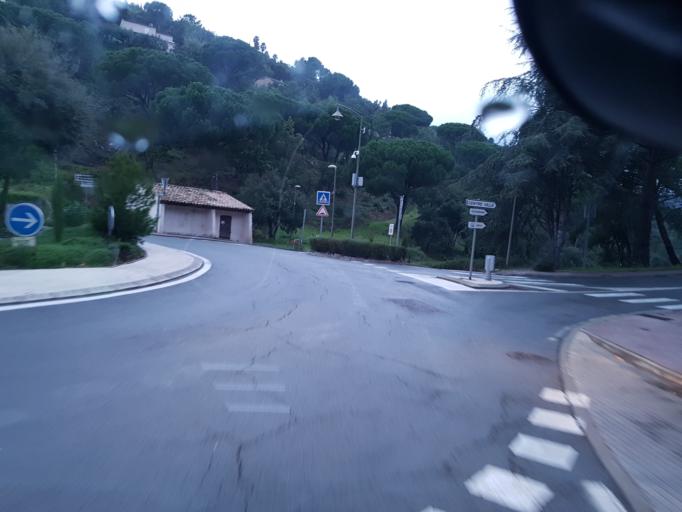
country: FR
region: Provence-Alpes-Cote d'Azur
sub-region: Departement du Var
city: Grimaud
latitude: 43.2767
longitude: 6.5166
